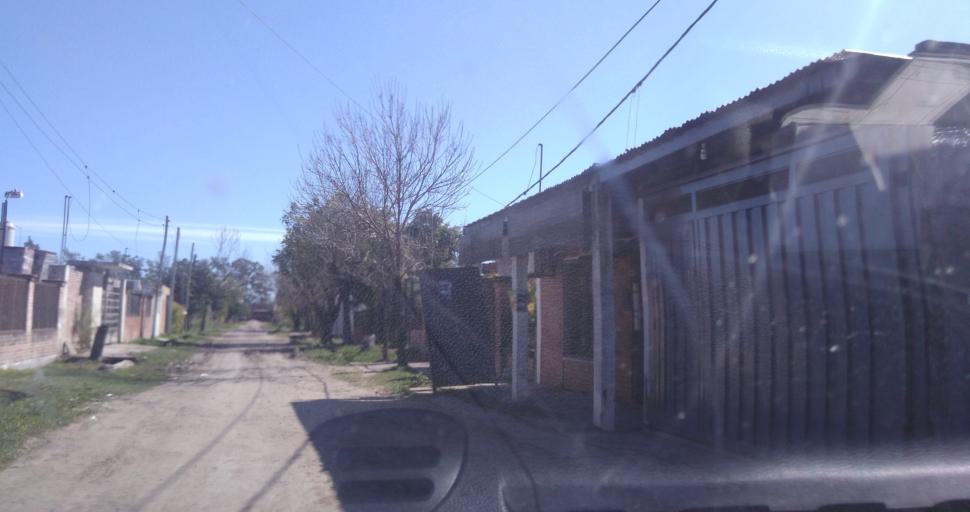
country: AR
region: Chaco
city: Fontana
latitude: -27.4438
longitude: -59.0298
